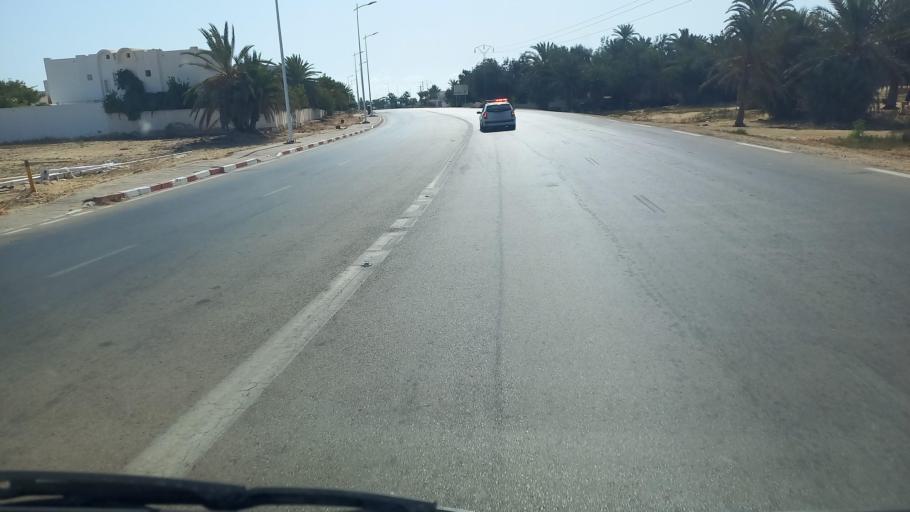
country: TN
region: Madanin
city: Midoun
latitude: 33.8372
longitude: 10.9967
